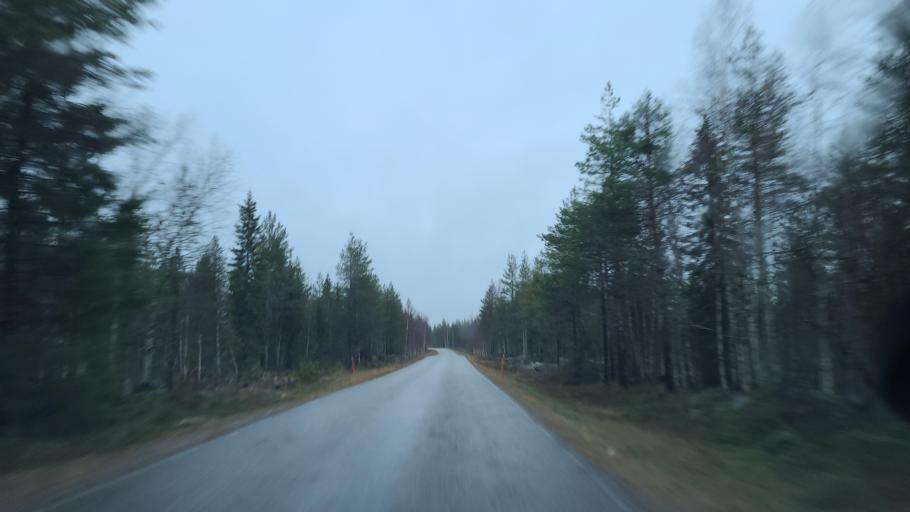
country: FI
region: Lapland
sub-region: Kemi-Tornio
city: Simo
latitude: 65.9225
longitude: 25.2010
